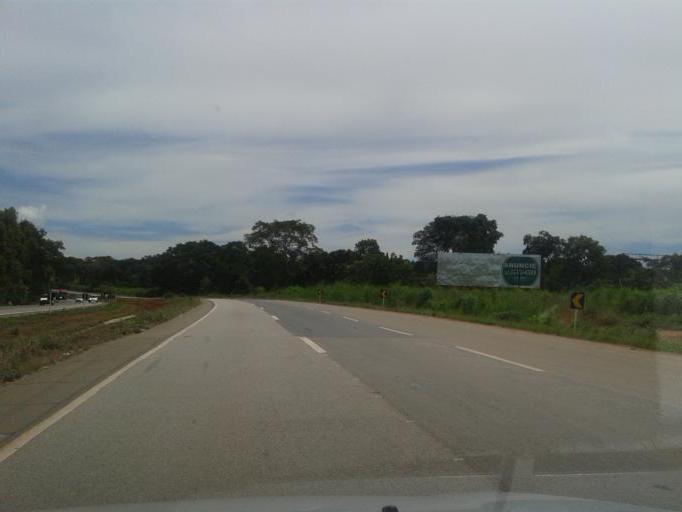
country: BR
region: Goias
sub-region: Hidrolandia
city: Hidrolandia
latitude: -17.0097
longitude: -49.2200
